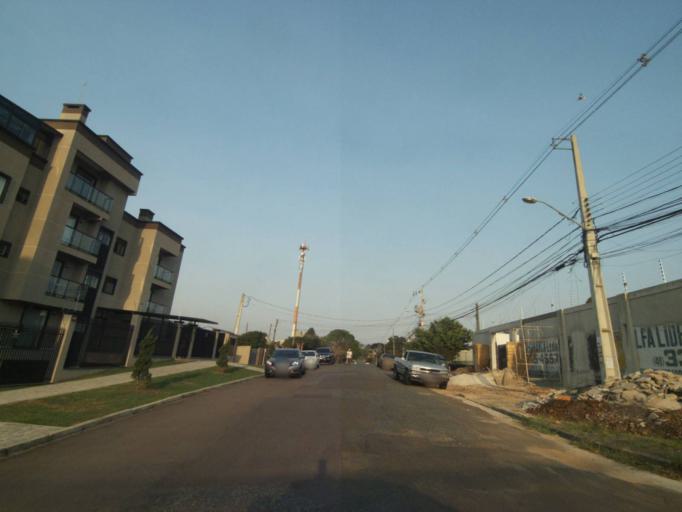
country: BR
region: Parana
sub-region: Curitiba
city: Curitiba
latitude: -25.4752
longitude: -49.3156
